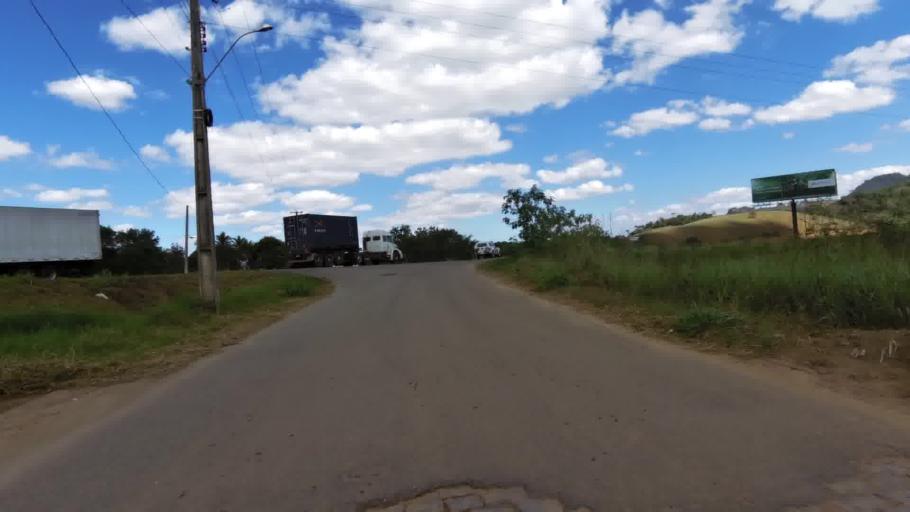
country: BR
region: Espirito Santo
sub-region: Rio Novo Do Sul
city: Rio Novo do Sul
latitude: -20.8719
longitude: -40.9470
